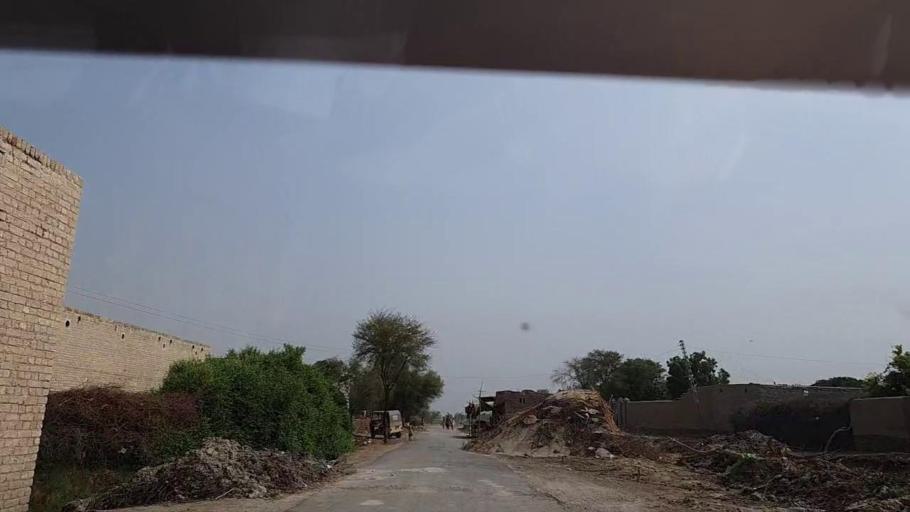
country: PK
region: Sindh
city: Khairpur Nathan Shah
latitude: 27.0652
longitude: 67.6875
